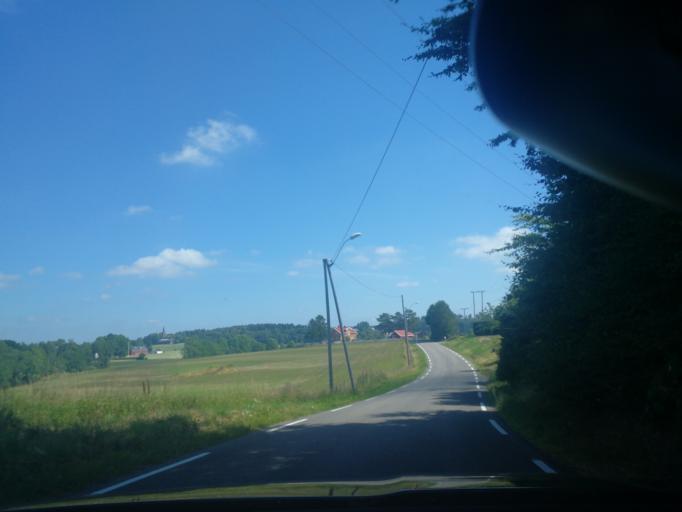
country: NO
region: Vestfold
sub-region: Stokke
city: Stokke
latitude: 59.2111
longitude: 10.2879
